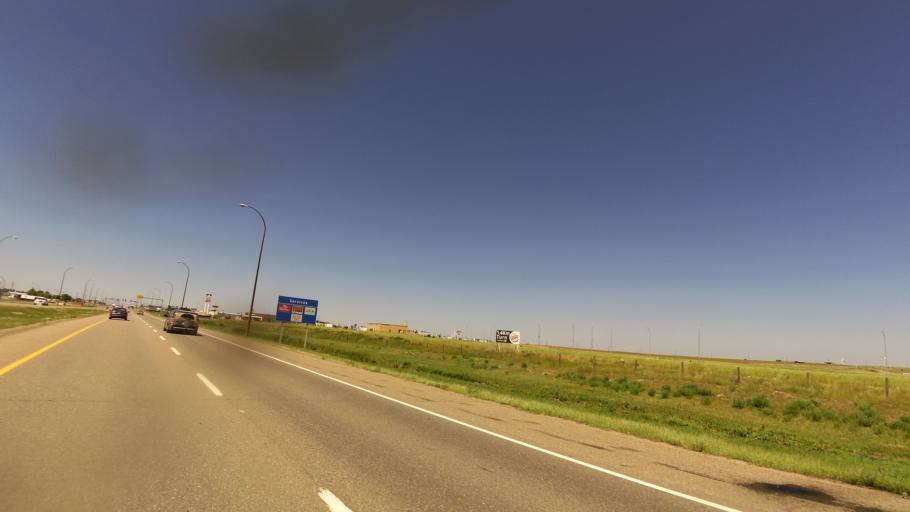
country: CA
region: Alberta
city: Medicine Hat
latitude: 50.0684
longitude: -110.7498
